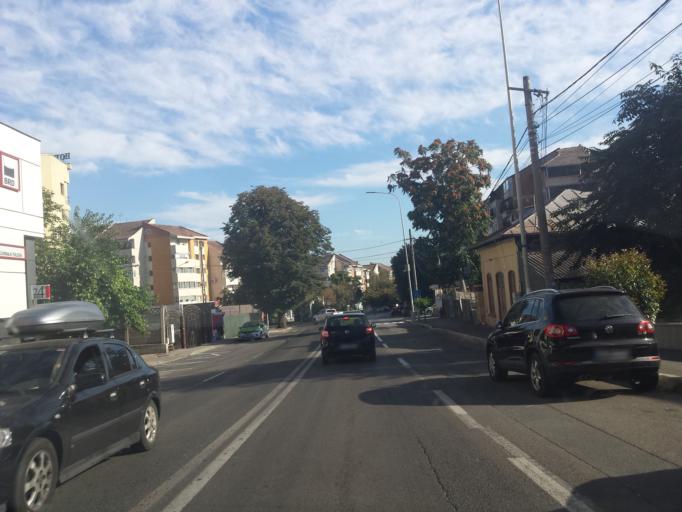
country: RO
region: Tulcea
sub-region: Municipiul Tulcea
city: Tulcea
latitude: 45.1707
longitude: 28.7977
